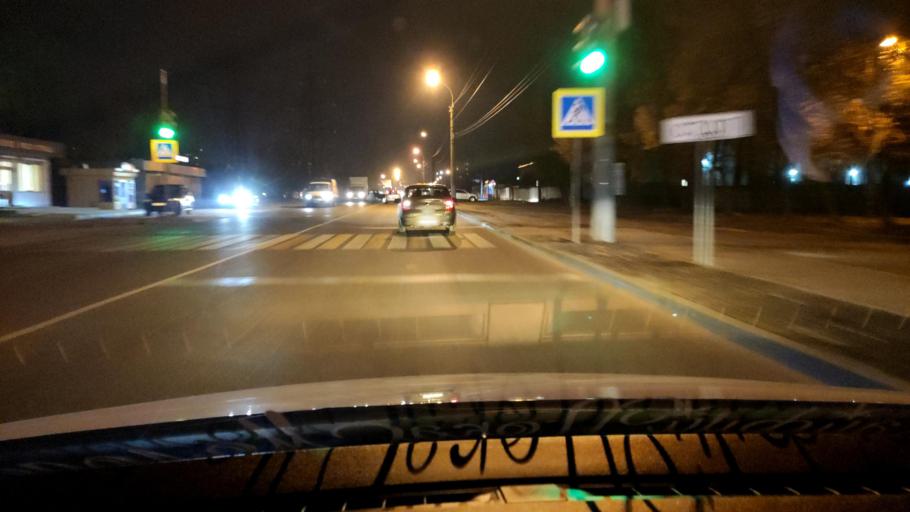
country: RU
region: Voronezj
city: Voronezh
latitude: 51.6412
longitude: 39.1583
